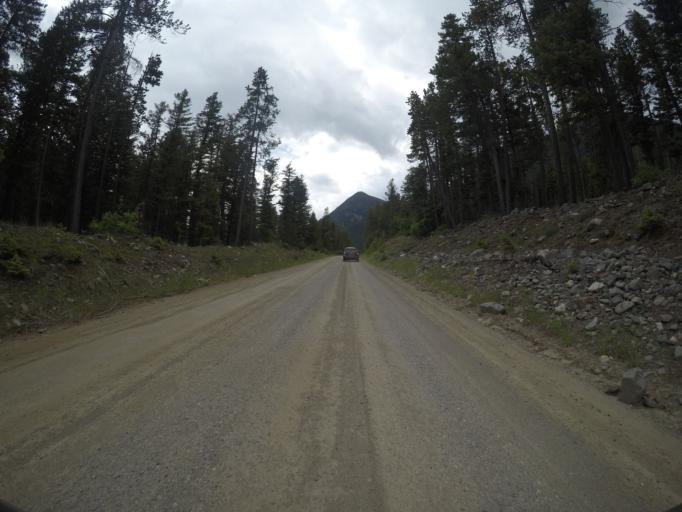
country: US
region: Montana
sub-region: Park County
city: Livingston
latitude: 45.4988
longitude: -110.2266
